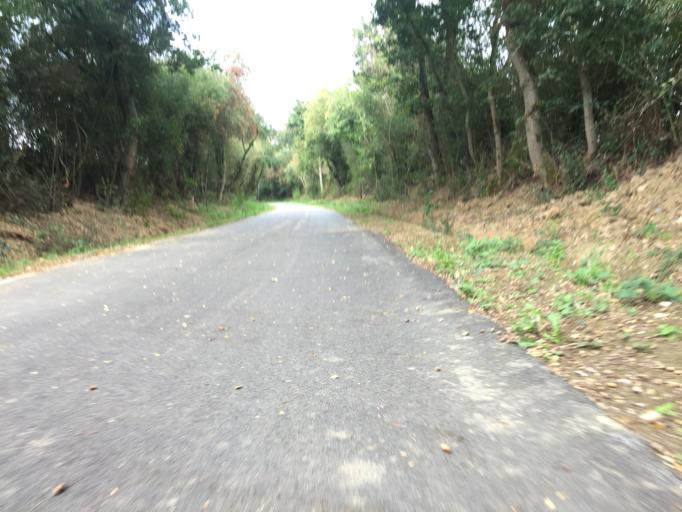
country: FR
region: Picardie
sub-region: Departement de l'Oise
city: Auneuil
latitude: 49.3945
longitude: 2.0130
